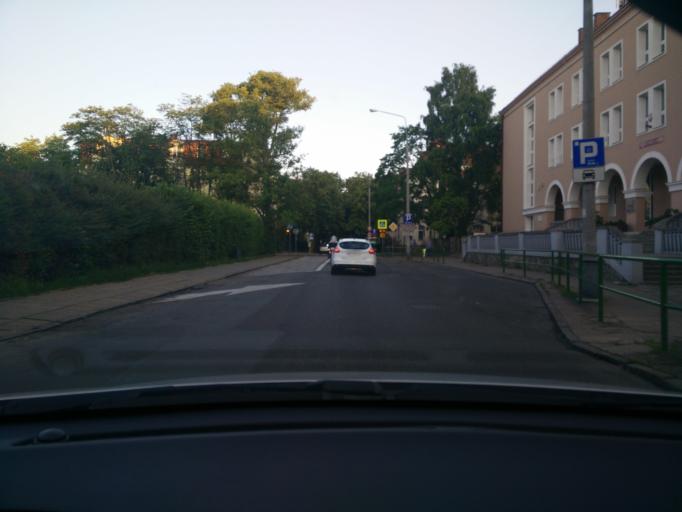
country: PL
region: Pomeranian Voivodeship
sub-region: Sopot
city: Sopot
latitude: 54.4494
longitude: 18.5627
